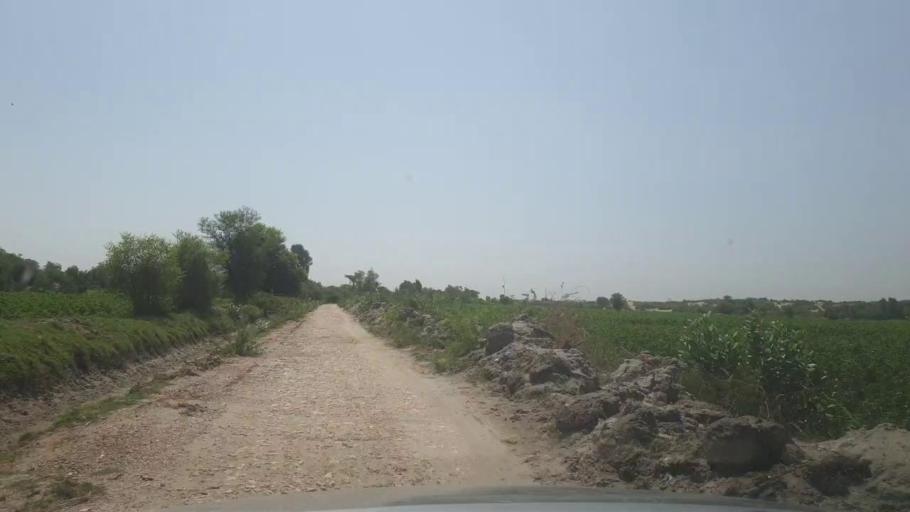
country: PK
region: Sindh
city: Khairpur
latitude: 27.3578
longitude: 69.0379
